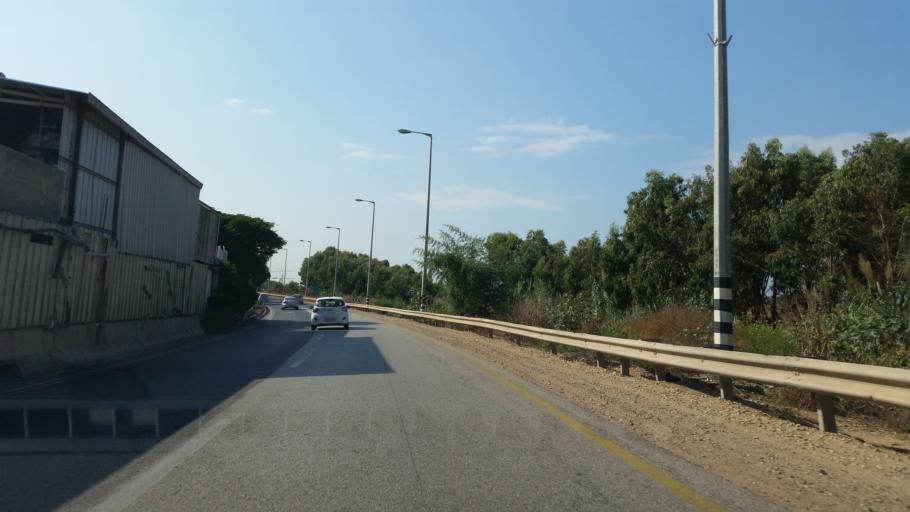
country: IL
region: Tel Aviv
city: Herzliya Pituah
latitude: 32.1560
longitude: 34.8076
